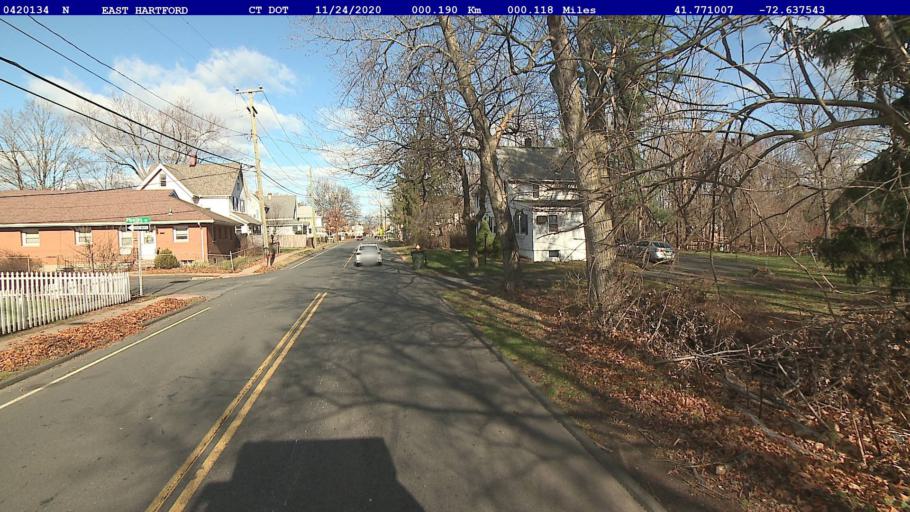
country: US
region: Connecticut
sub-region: Hartford County
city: East Hartford
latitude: 41.7710
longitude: -72.6375
